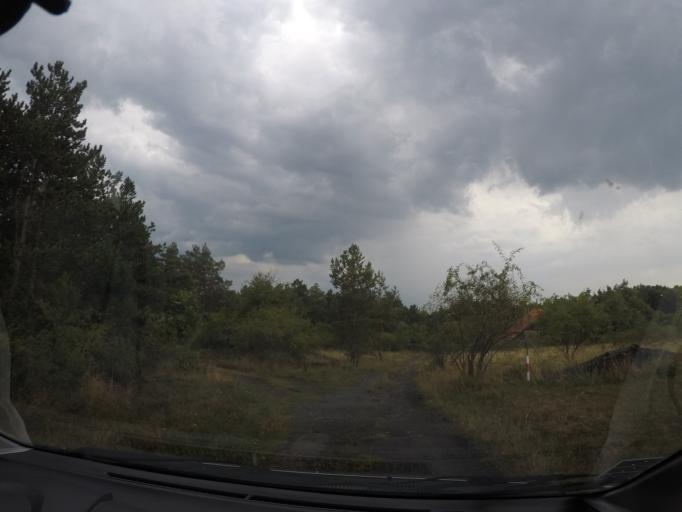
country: SK
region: Nitriansky
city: Tlmace
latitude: 48.3037
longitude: 18.5694
